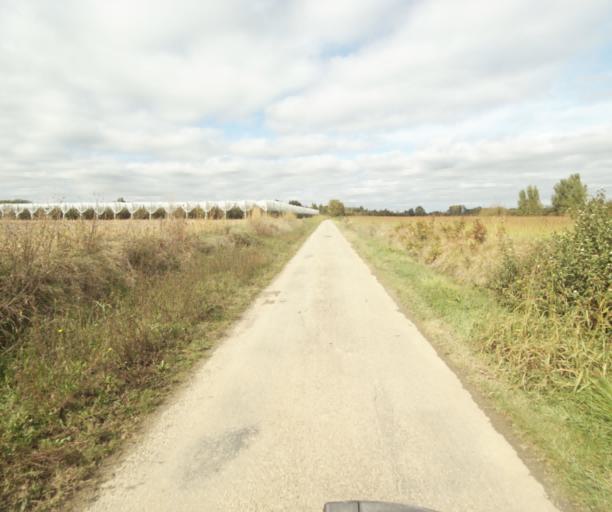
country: FR
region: Midi-Pyrenees
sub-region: Departement du Tarn-et-Garonne
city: Finhan
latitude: 43.9193
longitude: 1.2090
